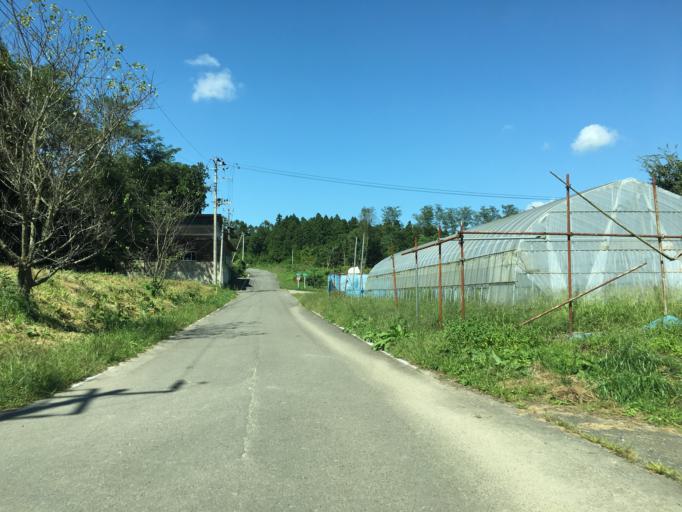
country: JP
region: Fukushima
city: Ishikawa
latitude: 37.2645
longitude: 140.5508
